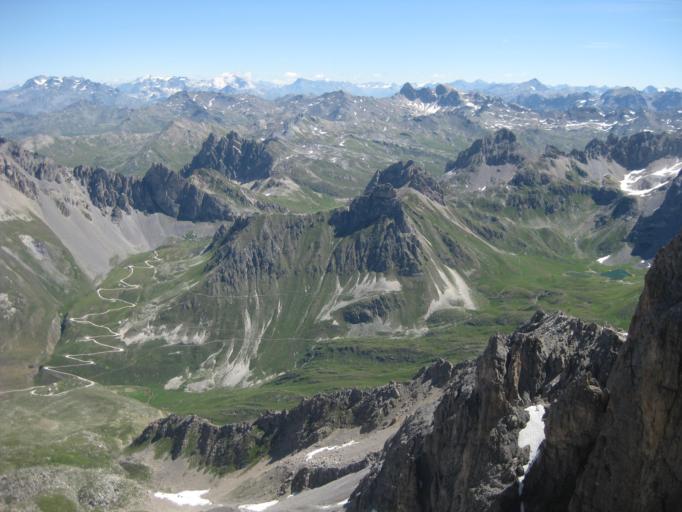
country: FR
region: Rhone-Alpes
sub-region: Departement de la Savoie
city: Valloire
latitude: 45.0631
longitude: 6.4356
